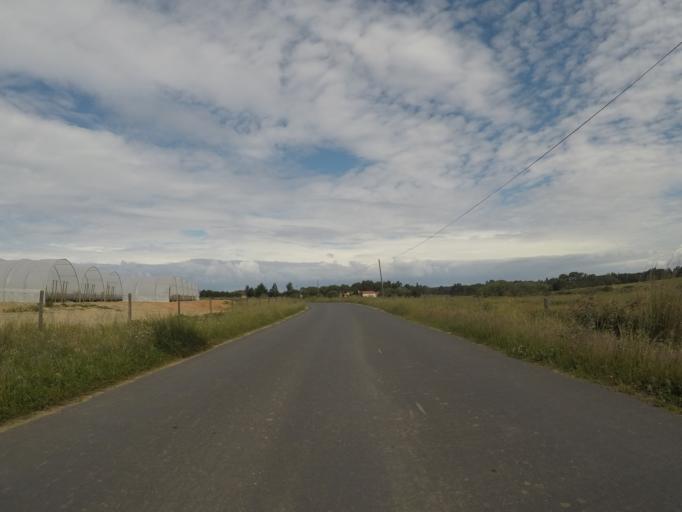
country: PT
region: Beja
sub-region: Odemira
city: Sao Teotonio
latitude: 37.4890
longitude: -8.7761
